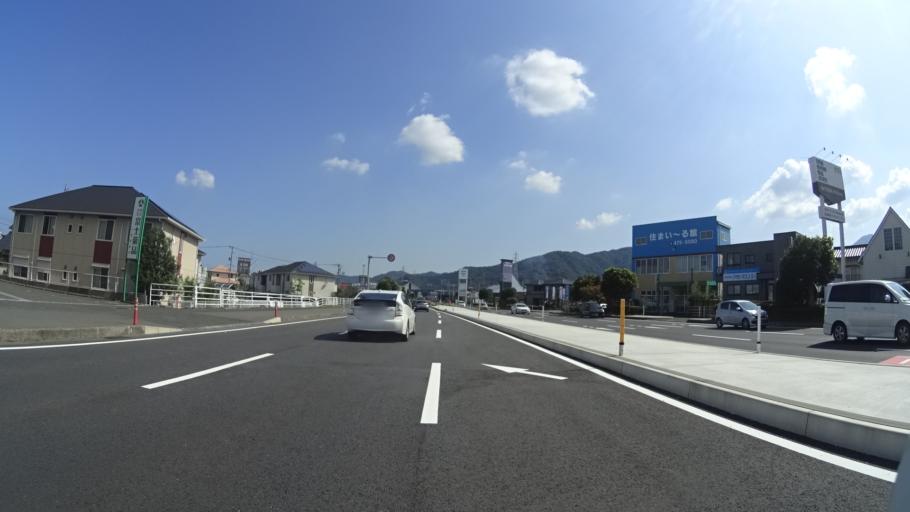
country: JP
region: Fukuoka
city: Kanda
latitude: 33.8179
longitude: 130.9359
